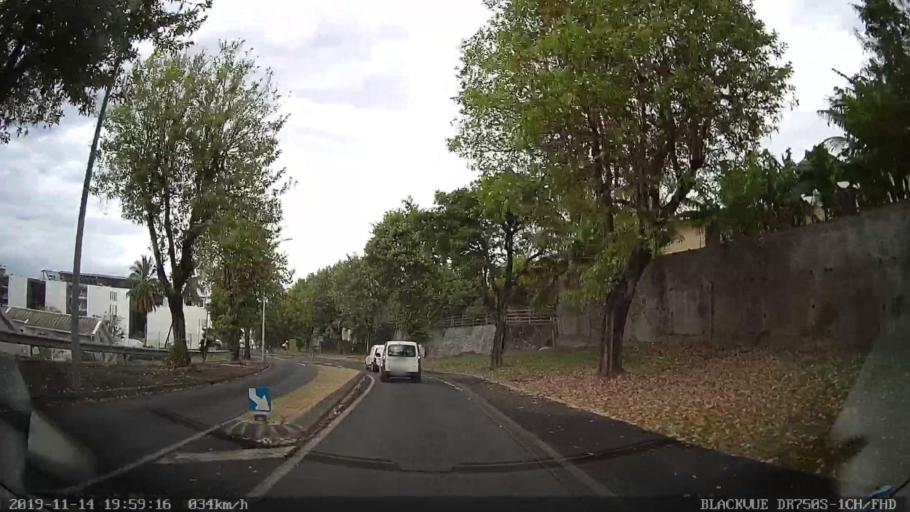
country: RE
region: Reunion
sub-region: Reunion
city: Saint-Denis
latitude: -20.9053
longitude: 55.4872
